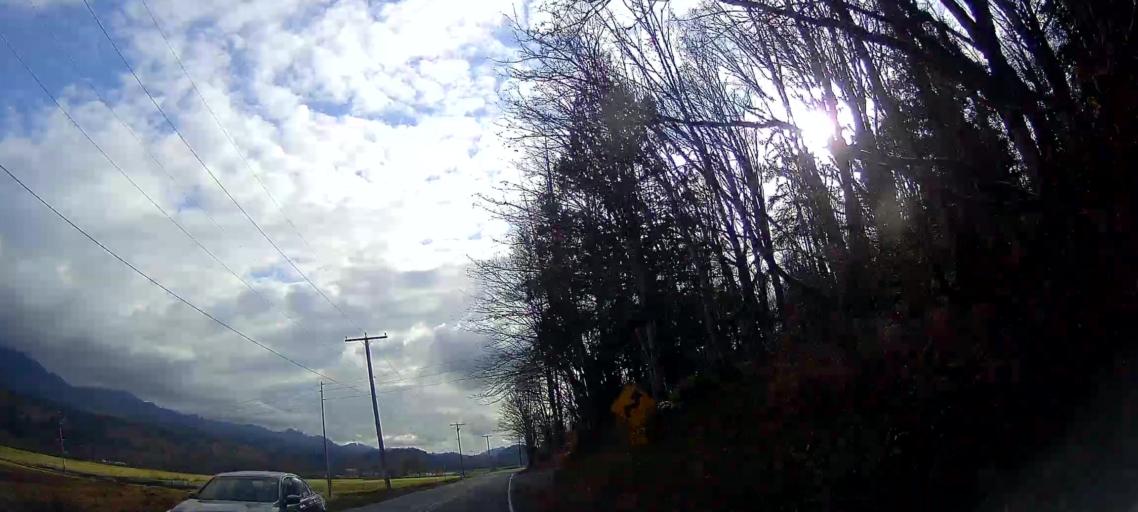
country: US
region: Washington
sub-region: Skagit County
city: Clear Lake
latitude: 48.4435
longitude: -122.2201
